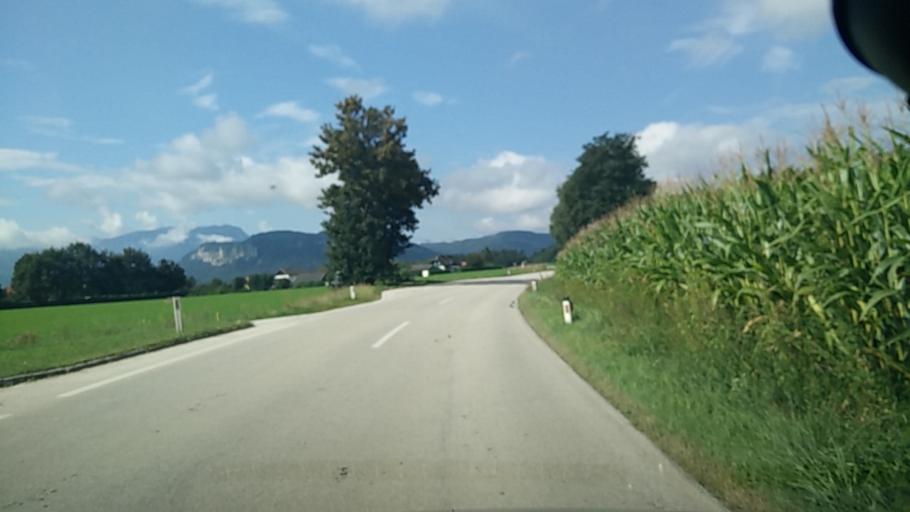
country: AT
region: Carinthia
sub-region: Politischer Bezirk Klagenfurt Land
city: Grafenstein
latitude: 46.6238
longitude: 14.5317
